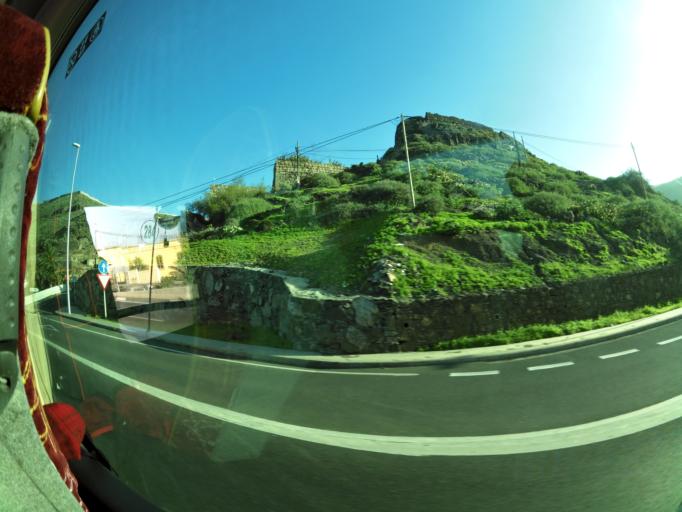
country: ES
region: Canary Islands
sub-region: Provincia de Las Palmas
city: Firgas
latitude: 28.1422
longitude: -15.5725
